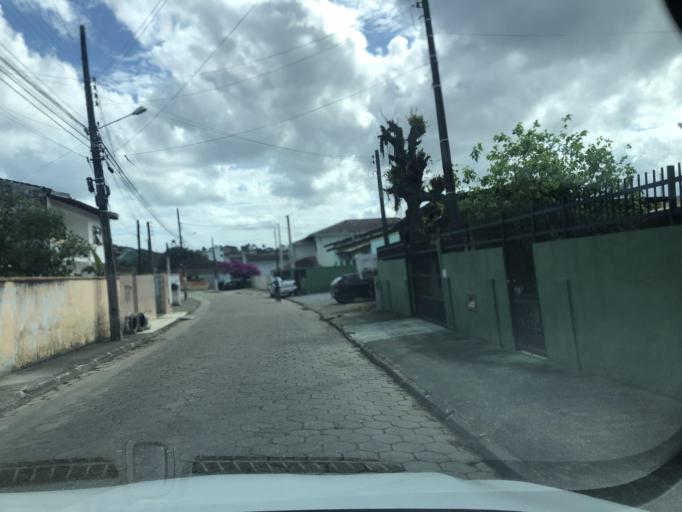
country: BR
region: Santa Catarina
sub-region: Sao Francisco Do Sul
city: Sao Francisco do Sul
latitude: -26.2443
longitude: -48.6270
